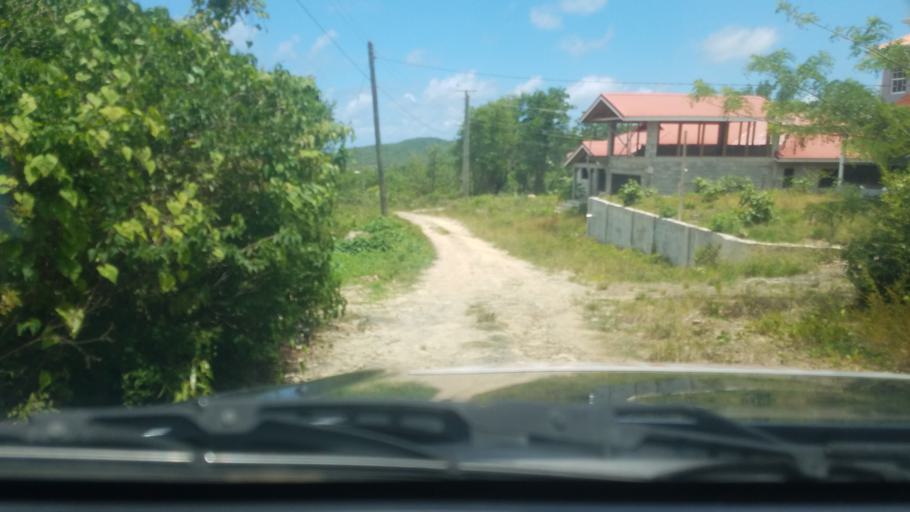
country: LC
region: Dennery Quarter
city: Dennery
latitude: 13.9206
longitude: -60.9014
